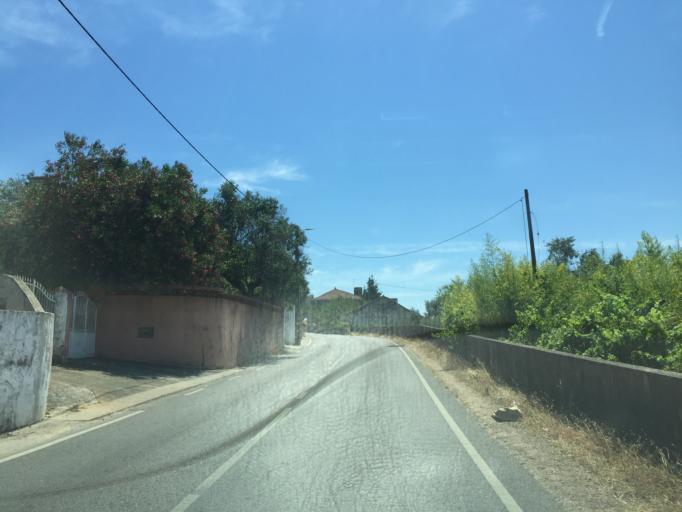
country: PT
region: Santarem
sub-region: Ferreira do Zezere
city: Ferreira do Zezere
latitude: 39.6007
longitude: -8.3043
